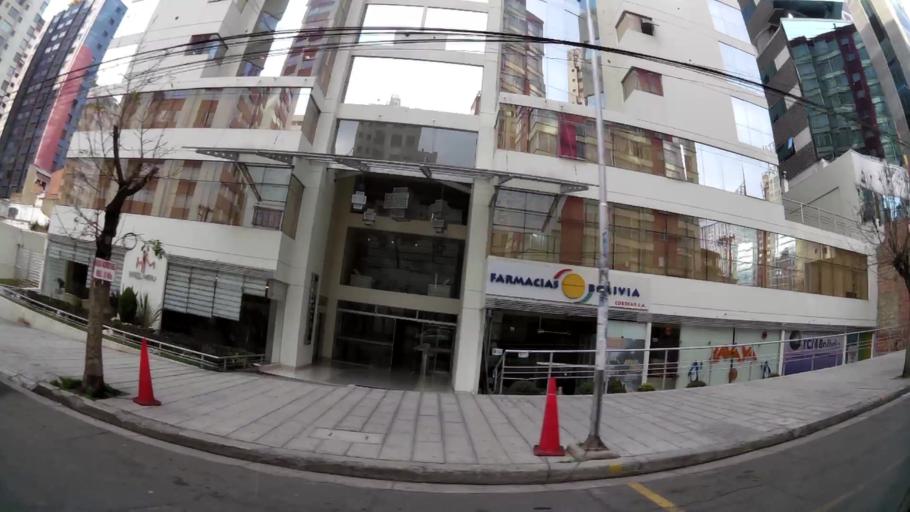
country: BO
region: La Paz
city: La Paz
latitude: -16.5120
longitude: -68.1234
